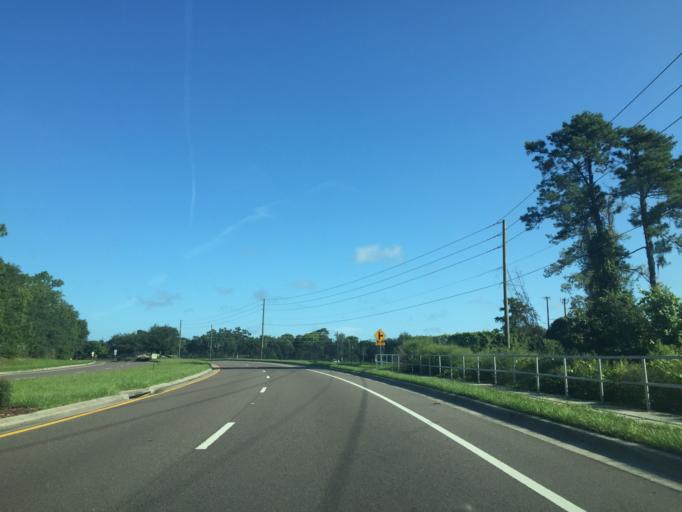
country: US
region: Florida
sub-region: Seminole County
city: Winter Springs
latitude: 28.6675
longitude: -81.2866
